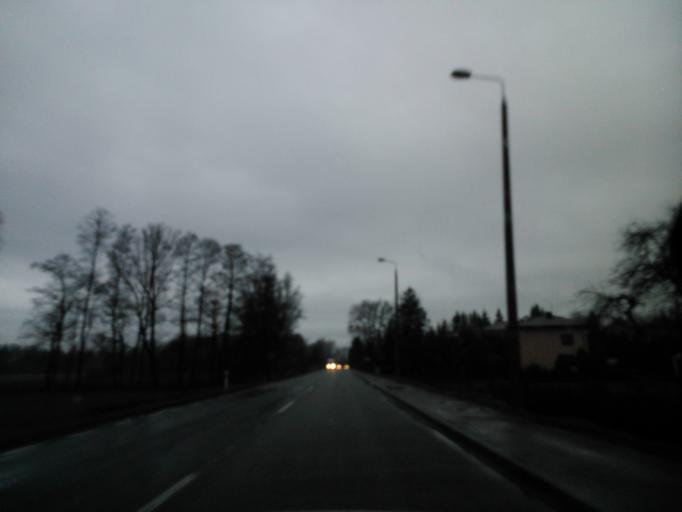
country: PL
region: Lublin Voivodeship
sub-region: Powiat krasnicki
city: Krasnik
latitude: 50.9104
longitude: 22.2574
